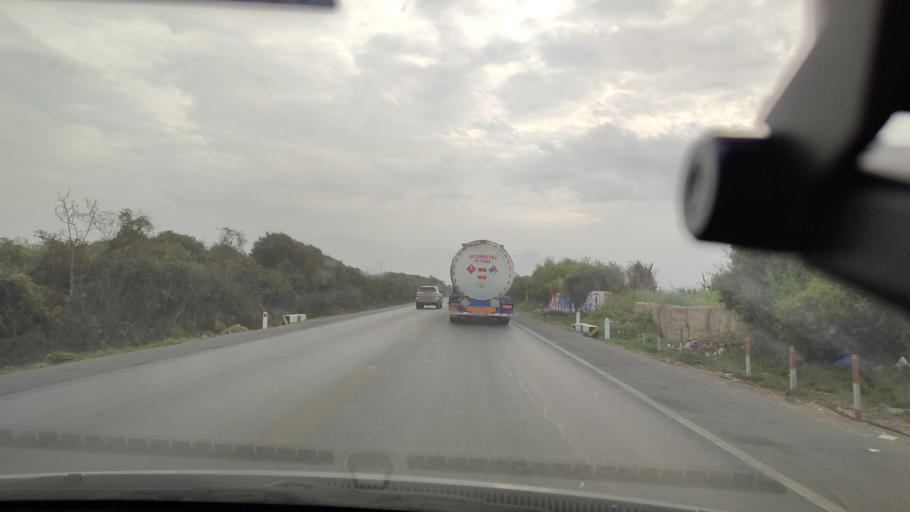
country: PE
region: La Libertad
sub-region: Provincia de Trujillo
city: Buenos Aires
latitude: -8.1482
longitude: -79.0316
